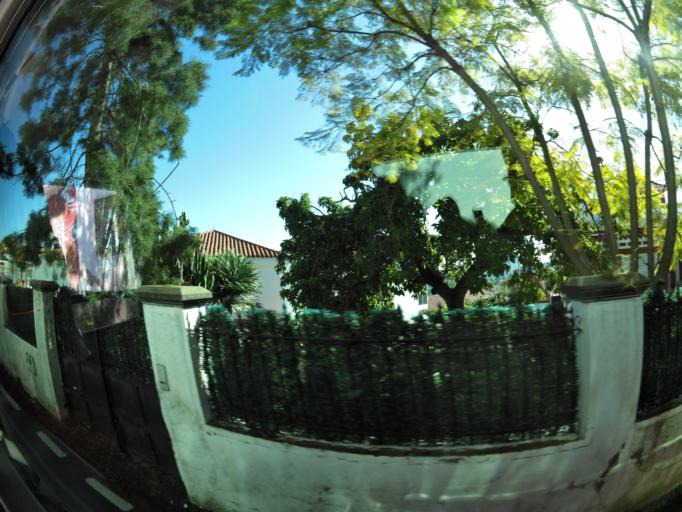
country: ES
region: Canary Islands
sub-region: Provincia de Las Palmas
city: Santa Brigida
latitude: 28.0450
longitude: -15.4748
